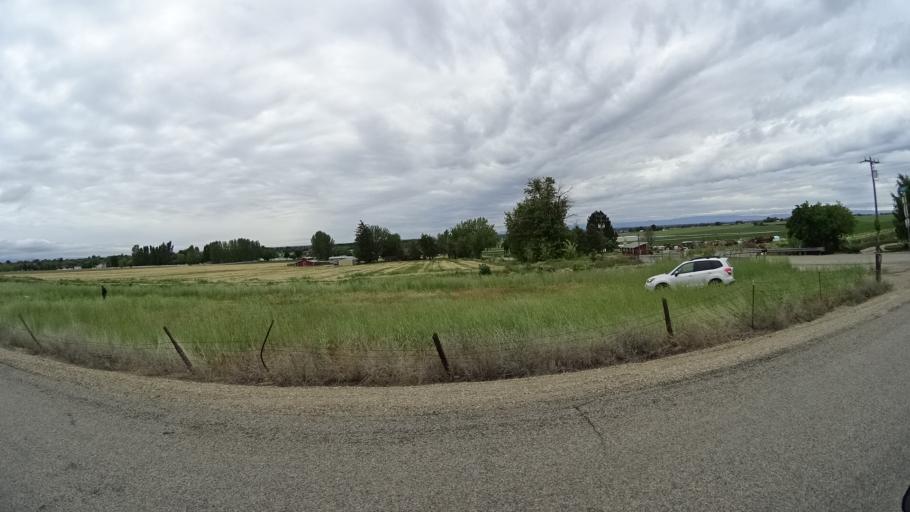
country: US
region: Idaho
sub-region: Ada County
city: Eagle
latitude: 43.7356
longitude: -116.4129
